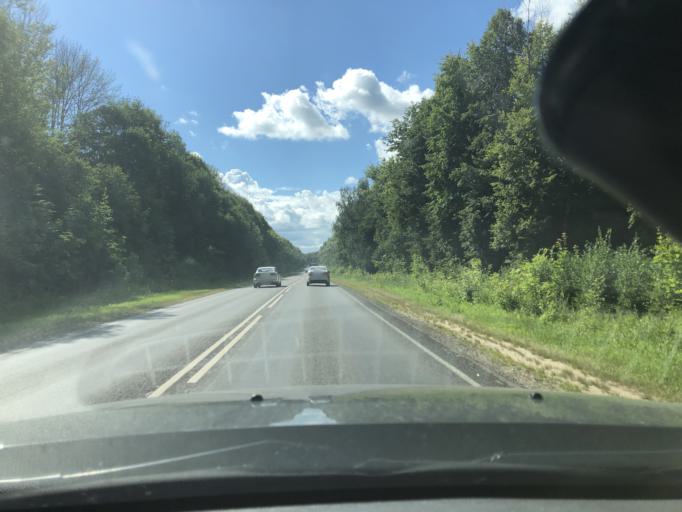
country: RU
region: Tula
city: Severo-Zadonsk
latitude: 53.9687
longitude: 38.4281
